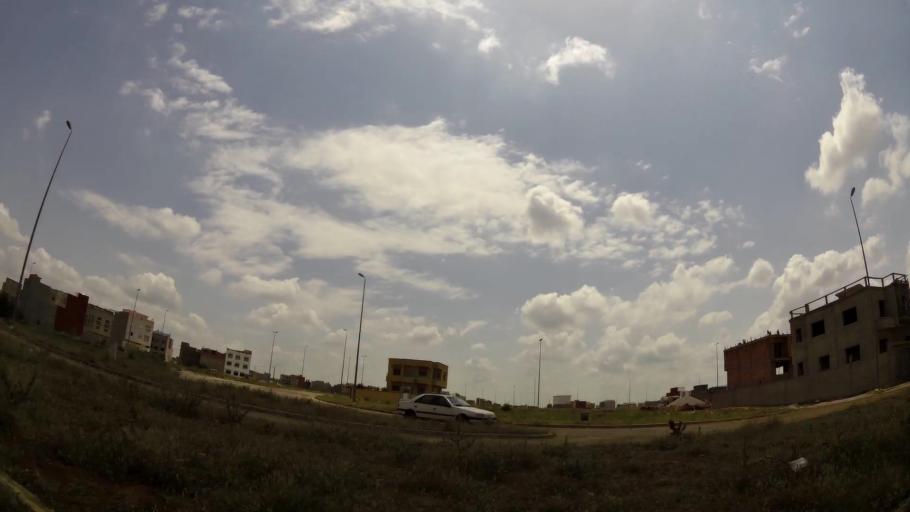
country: MA
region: Rabat-Sale-Zemmour-Zaer
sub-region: Khemisset
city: Tiflet
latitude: 34.0043
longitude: -6.5395
